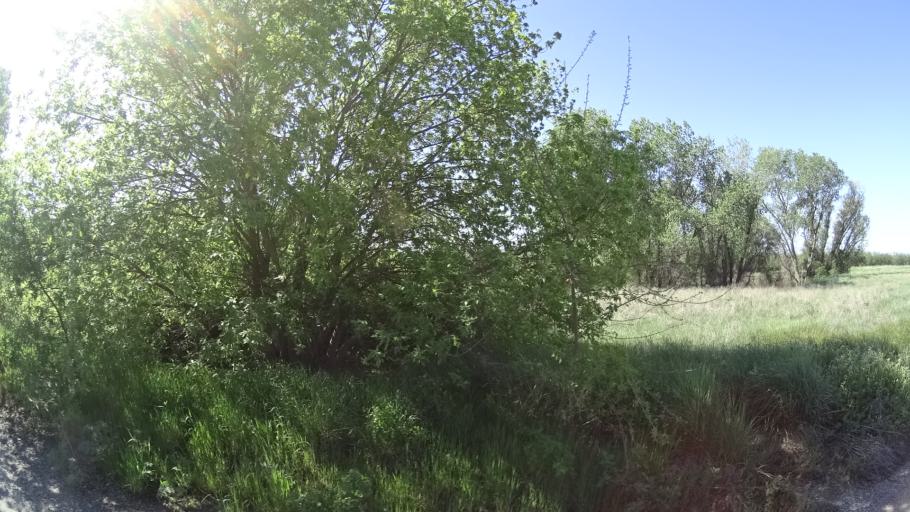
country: US
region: California
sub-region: Glenn County
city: Hamilton City
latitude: 39.7129
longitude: -121.9784
